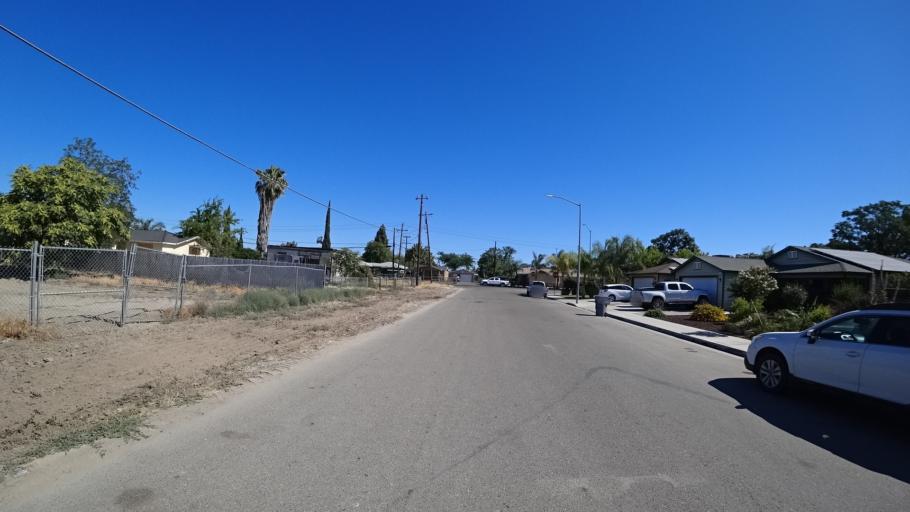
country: US
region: California
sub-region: Fresno County
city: Easton
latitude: 36.6917
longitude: -119.7953
